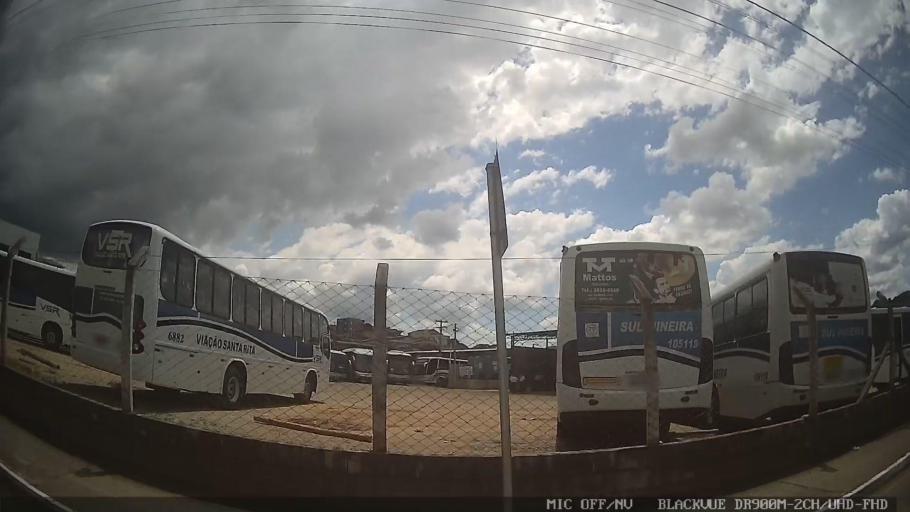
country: BR
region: Minas Gerais
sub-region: Extrema
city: Extrema
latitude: -22.8542
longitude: -46.3110
